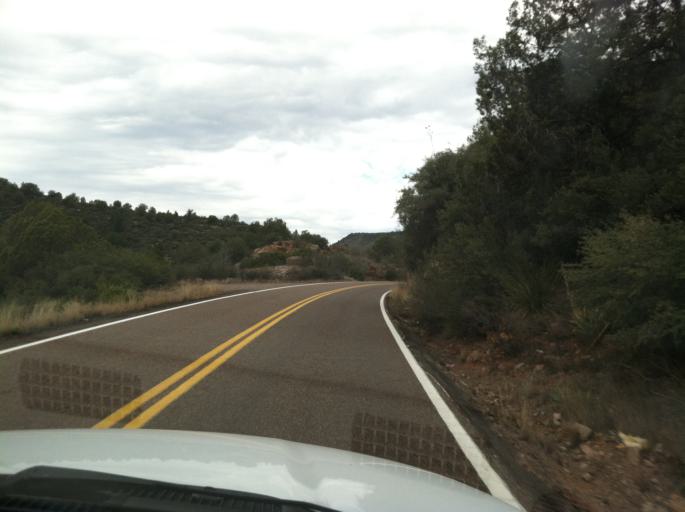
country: US
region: Arizona
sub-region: Gila County
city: Payson
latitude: 34.3054
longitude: -111.3599
